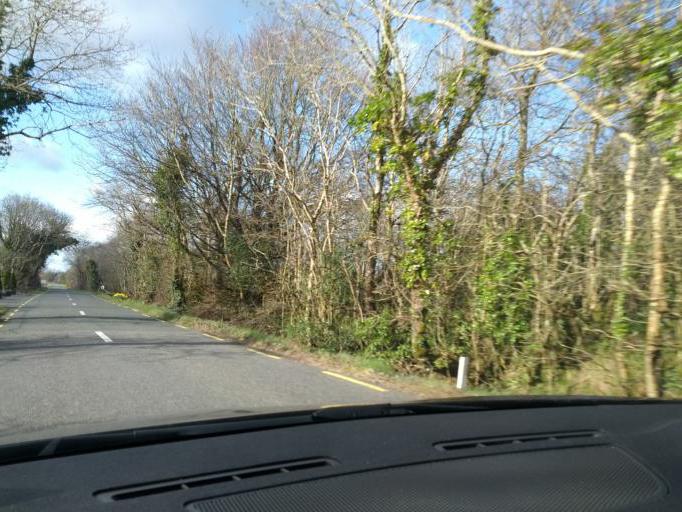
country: IE
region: Connaught
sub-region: County Galway
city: Athenry
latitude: 53.4994
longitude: -8.5698
